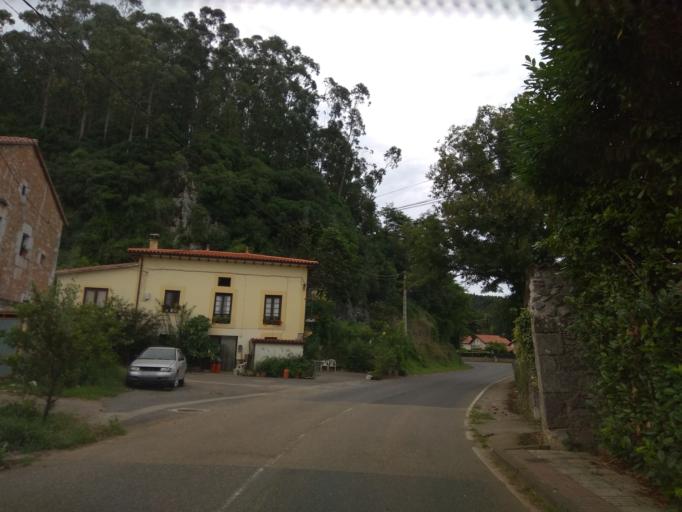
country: ES
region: Cantabria
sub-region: Provincia de Cantabria
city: Hazas de Cesto
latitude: 43.4000
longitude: -3.5978
